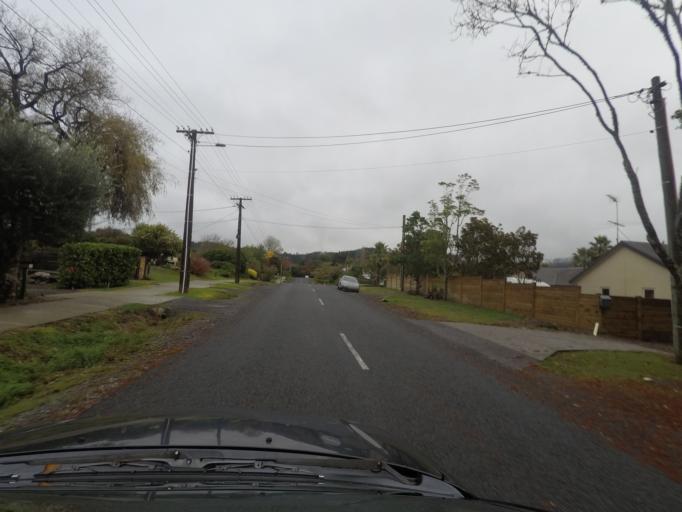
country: NZ
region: Auckland
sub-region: Auckland
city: Rosebank
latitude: -36.7559
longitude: 174.5965
